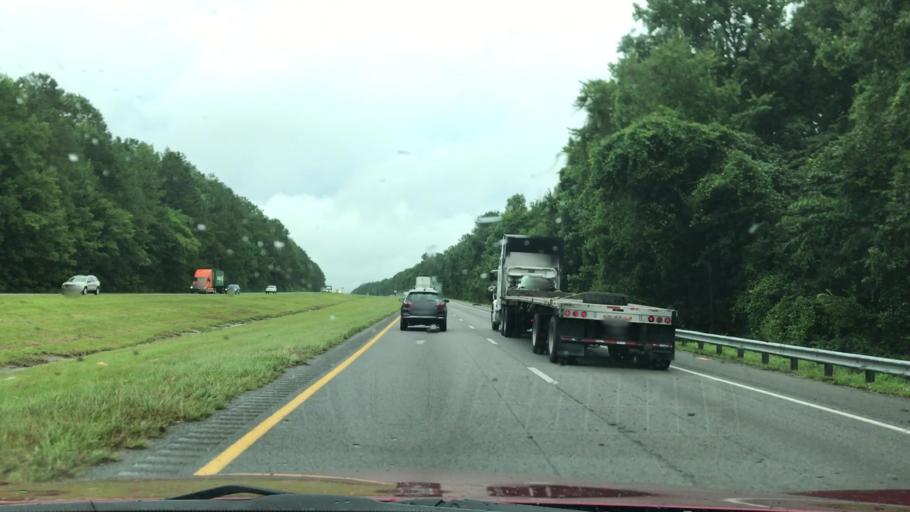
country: US
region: South Carolina
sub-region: Dorchester County
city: Ridgeville
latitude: 33.0950
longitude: -80.2337
